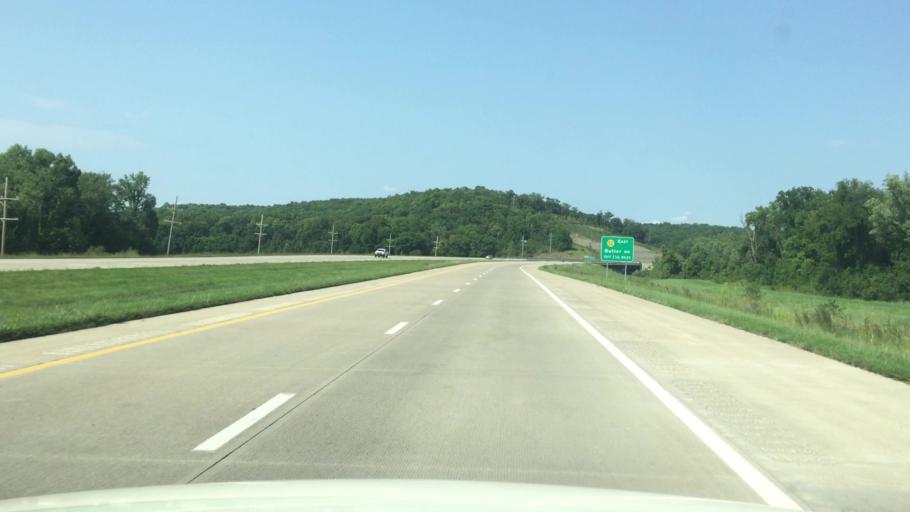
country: US
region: Kansas
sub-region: Linn County
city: Pleasanton
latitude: 38.2451
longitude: -94.6881
